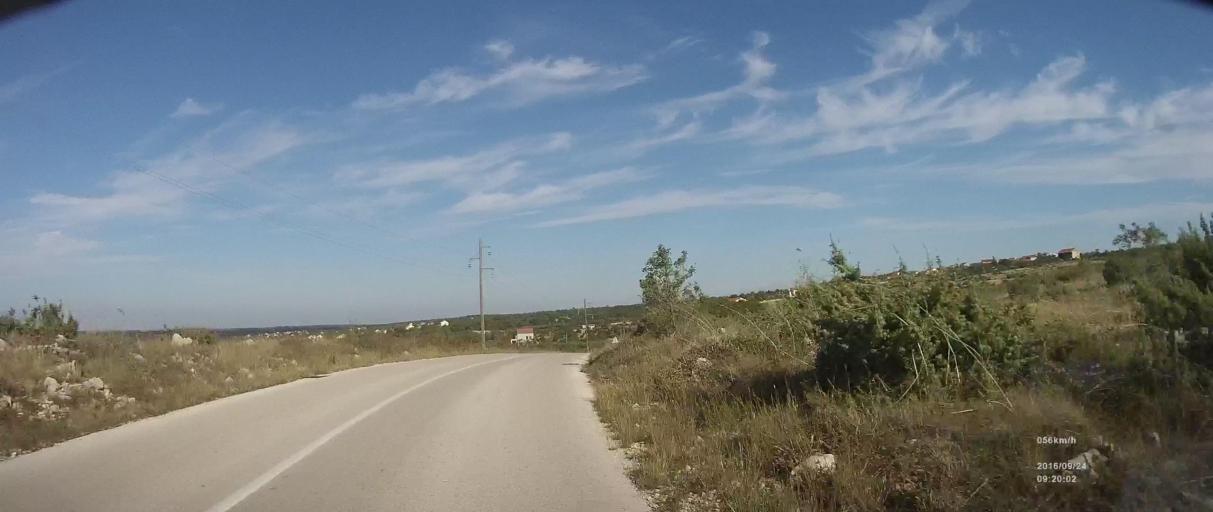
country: HR
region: Zadarska
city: Polaca
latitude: 44.0658
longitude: 15.4992
